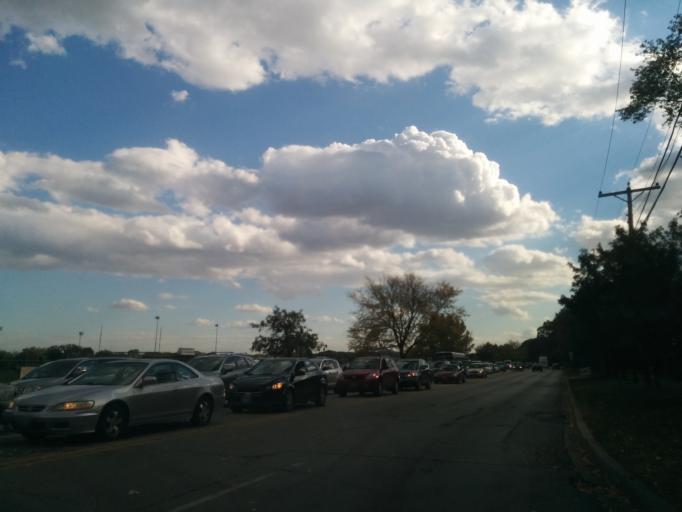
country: US
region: Illinois
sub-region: Cook County
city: Park Ridge
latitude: 42.0059
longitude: -87.8555
